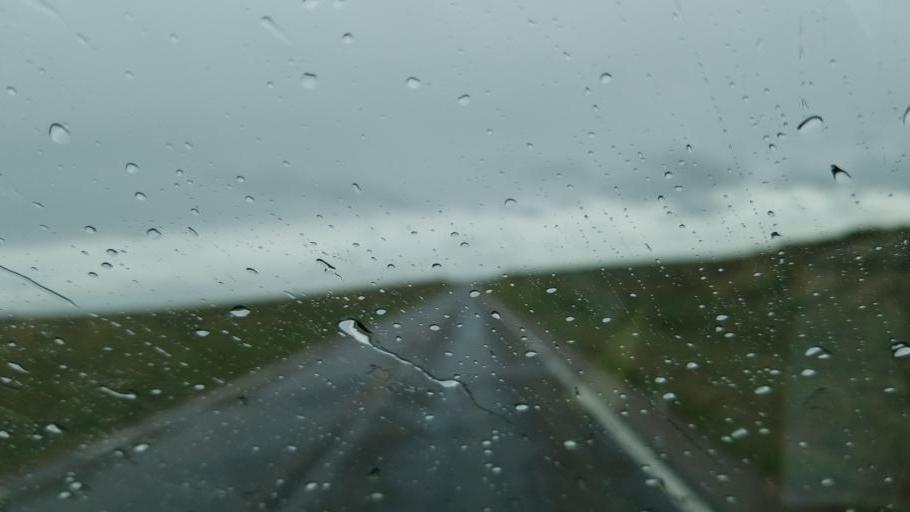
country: US
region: Colorado
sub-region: Lincoln County
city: Hugo
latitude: 38.8494
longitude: -103.2678
